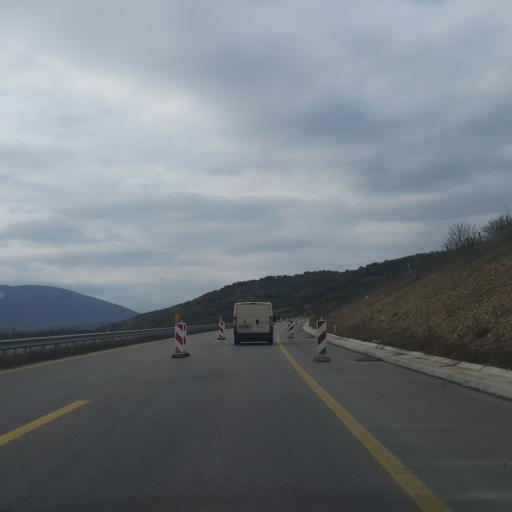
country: RS
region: Central Serbia
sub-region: Pirotski Okrug
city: Bela Palanka
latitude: 43.2371
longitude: 22.3417
